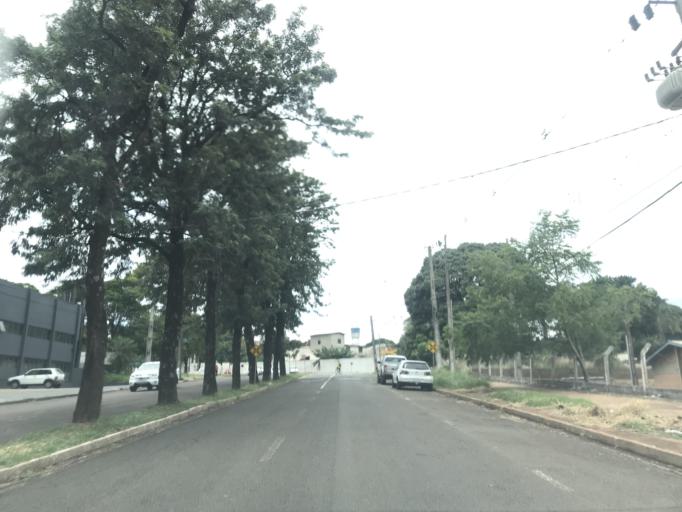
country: BR
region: Parana
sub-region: Maringa
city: Maringa
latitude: -23.4243
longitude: -51.9709
